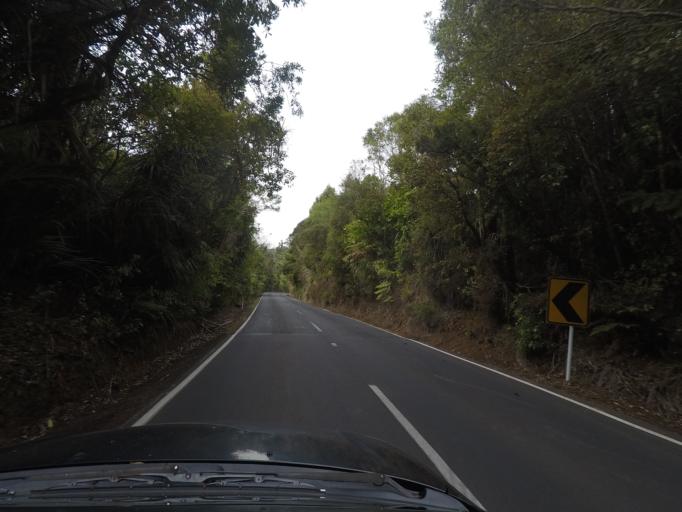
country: NZ
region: Auckland
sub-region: Auckland
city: Titirangi
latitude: -36.9426
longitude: 174.5913
